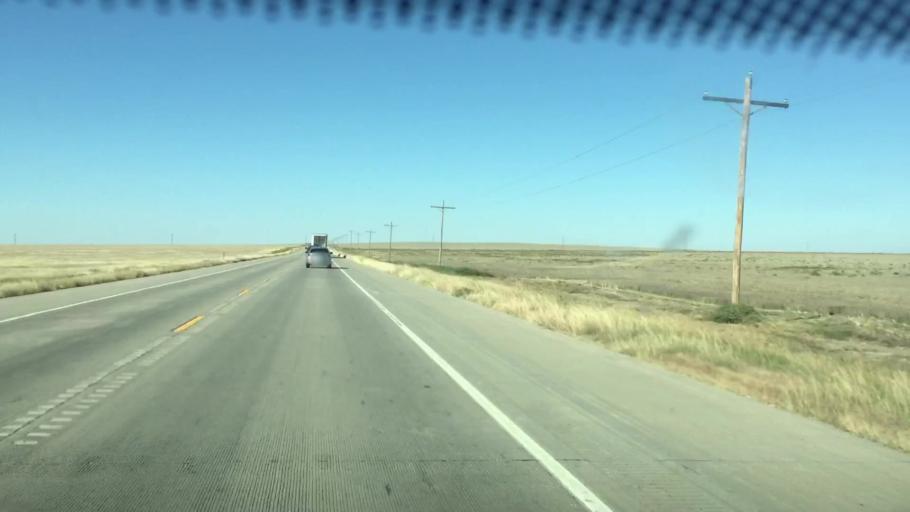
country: US
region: Colorado
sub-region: Prowers County
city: Lamar
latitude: 38.2479
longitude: -102.7240
